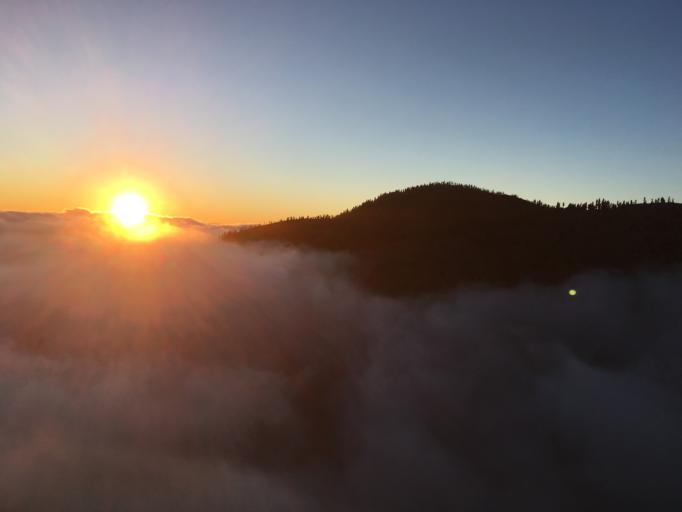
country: ES
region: Canary Islands
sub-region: Provincia de Santa Cruz de Tenerife
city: Vilaflor
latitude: 28.2055
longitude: -16.6834
